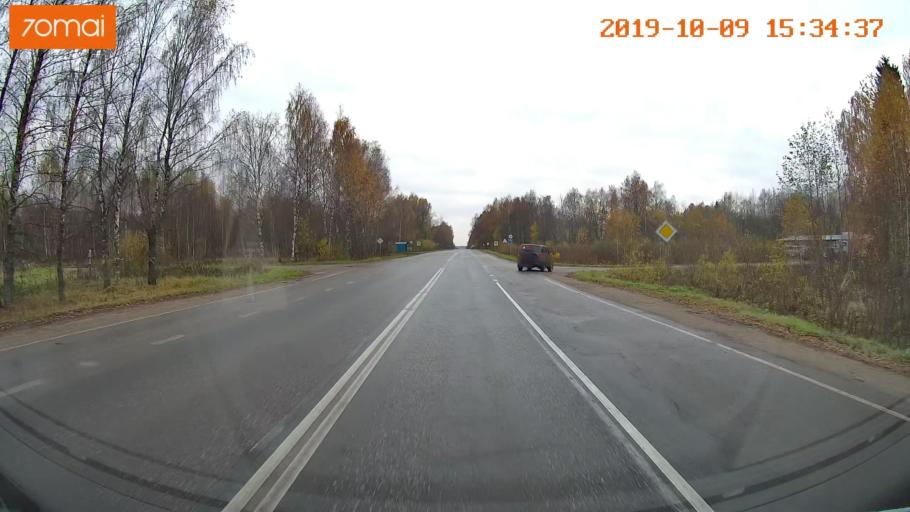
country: RU
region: Kostroma
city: Oktyabr'skiy
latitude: 57.9393
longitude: 41.2417
